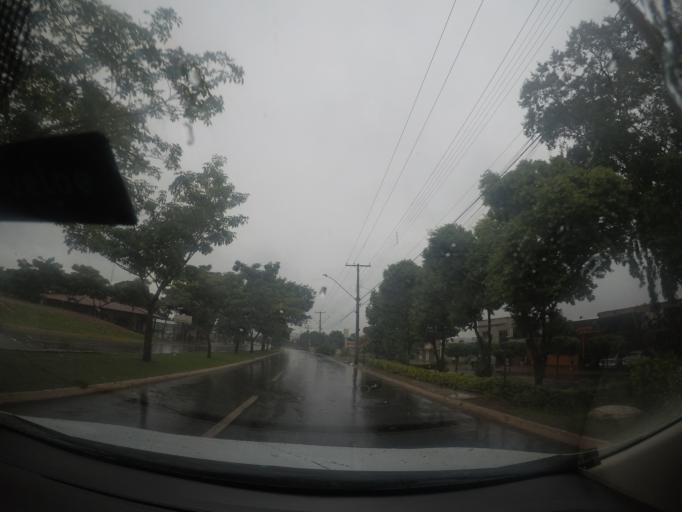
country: BR
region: Goias
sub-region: Goiania
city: Goiania
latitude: -16.6032
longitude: -49.3339
